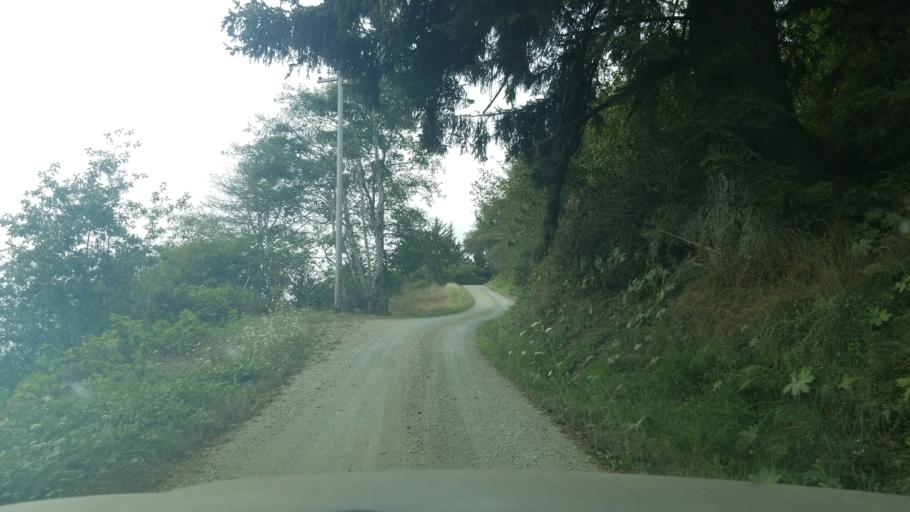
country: US
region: California
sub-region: Del Norte County
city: Bertsch-Oceanview
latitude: 41.5231
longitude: -124.0785
